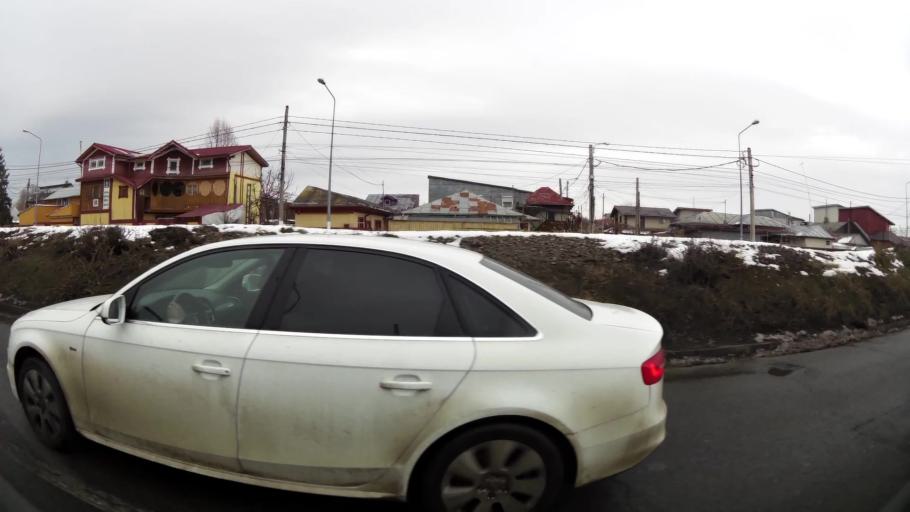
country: RO
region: Ilfov
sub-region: Comuna Pantelimon
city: Pantelimon
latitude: 44.4314
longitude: 26.1961
